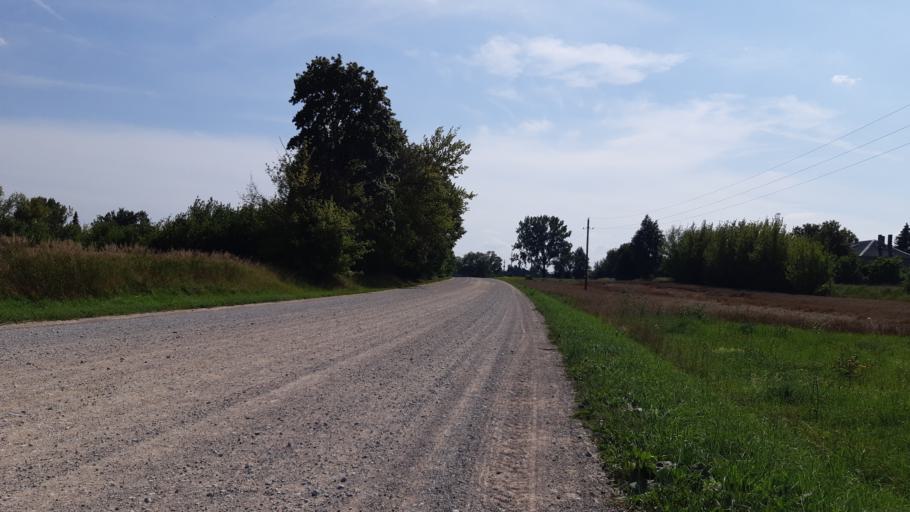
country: LT
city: Virbalis
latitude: 54.6328
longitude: 22.8263
